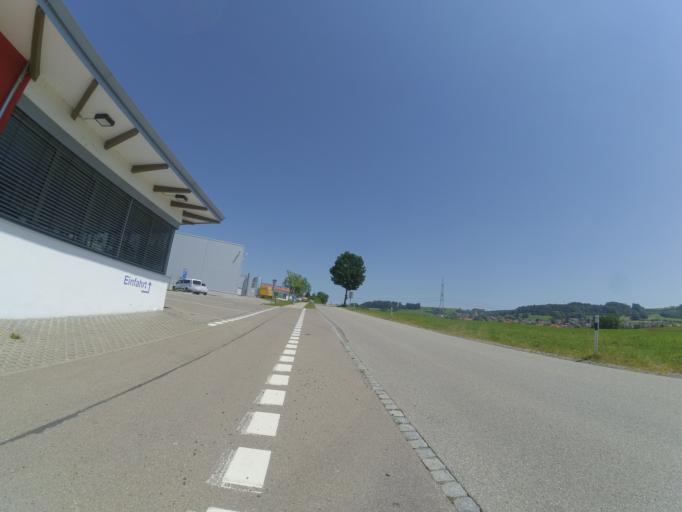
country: DE
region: Bavaria
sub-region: Swabia
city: Haldenwang
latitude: 47.7974
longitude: 10.3348
